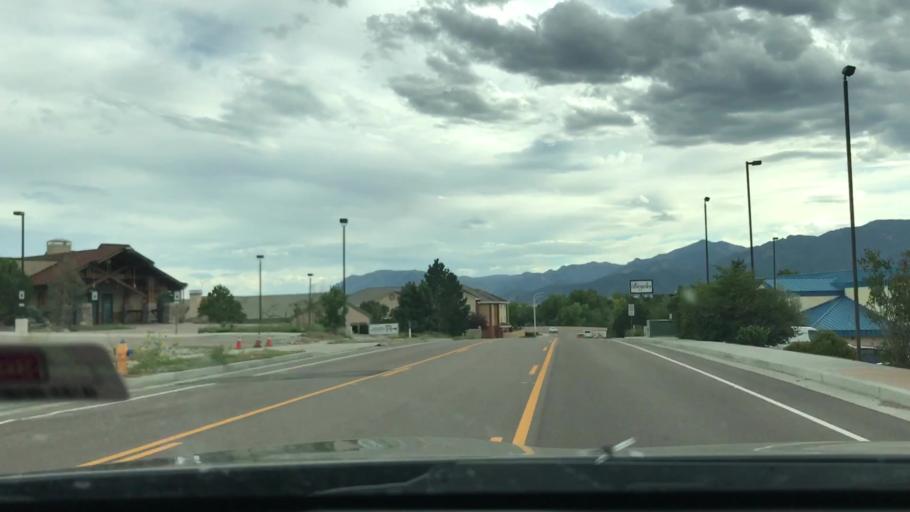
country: US
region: Colorado
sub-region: El Paso County
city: Colorado Springs
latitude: 38.9192
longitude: -104.8167
